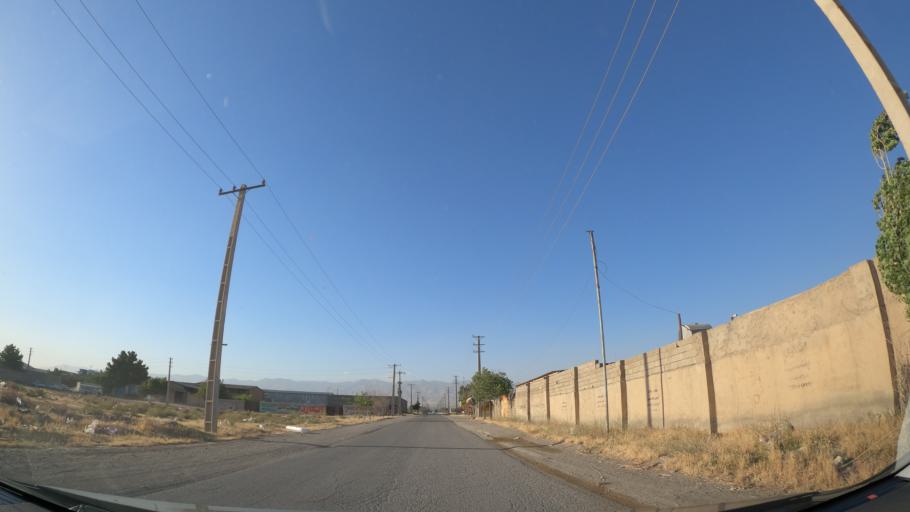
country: IR
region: Alborz
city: Hashtgerd
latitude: 35.9172
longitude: 50.7592
